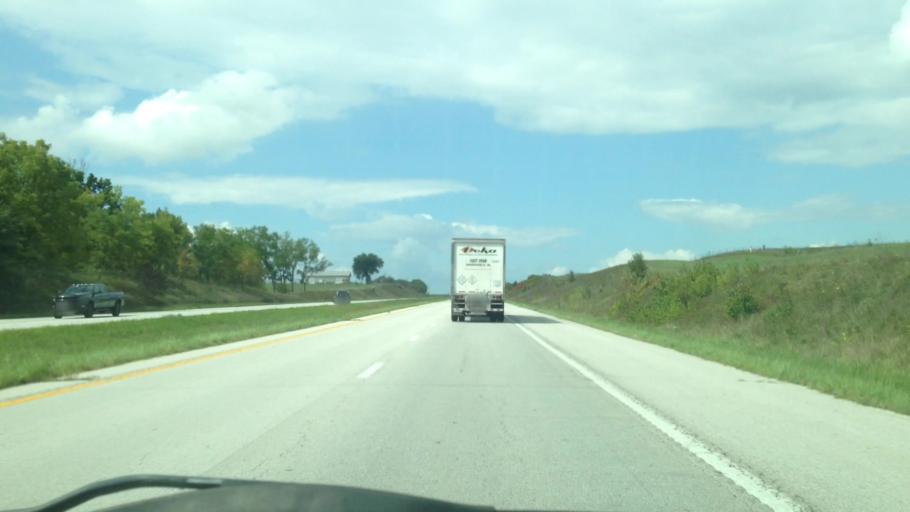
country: US
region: Missouri
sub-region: Marion County
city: Palmyra
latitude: 39.7734
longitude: -91.5192
